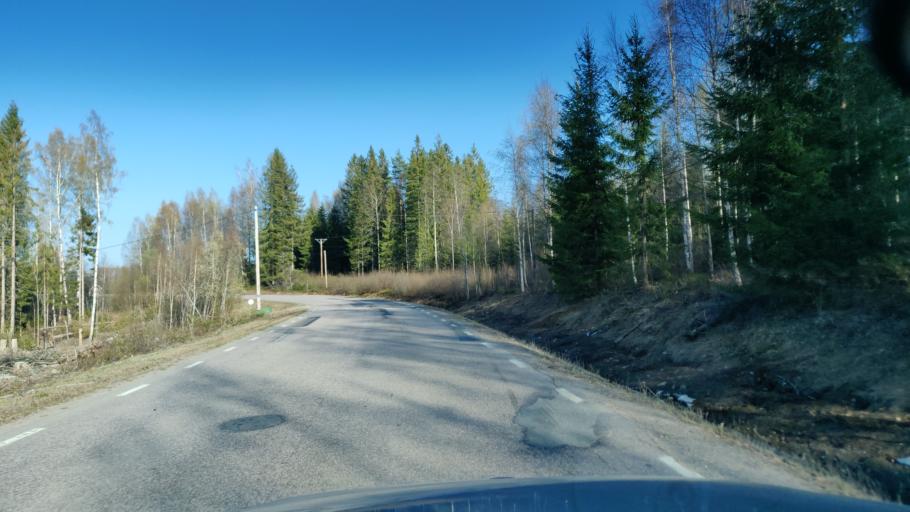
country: SE
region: Vaermland
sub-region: Munkfors Kommun
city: Munkfors
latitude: 59.9704
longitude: 13.4493
